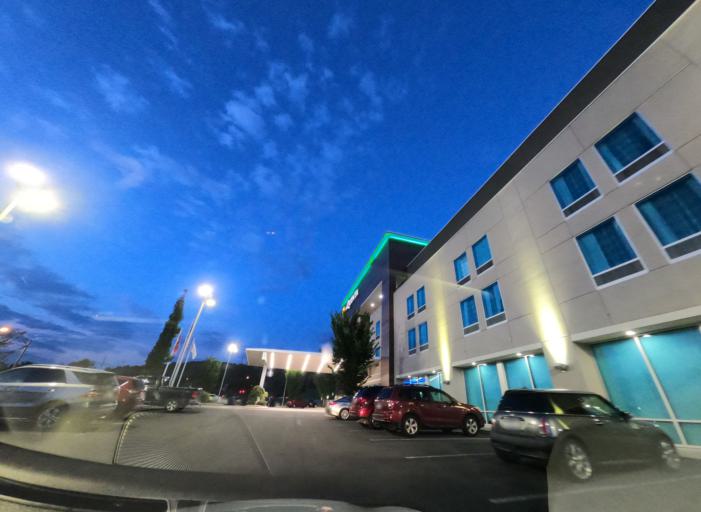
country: US
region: Tennessee
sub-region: Bradley County
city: Cleveland
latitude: 35.1940
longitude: -84.8902
